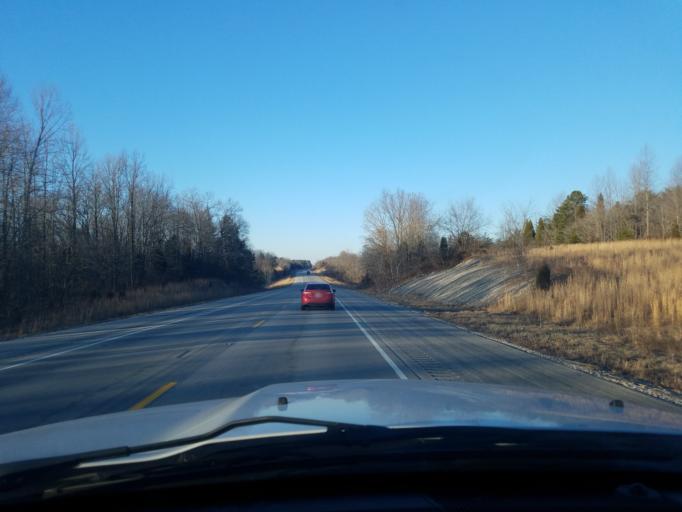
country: US
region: Indiana
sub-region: Crawford County
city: English
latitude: 38.1409
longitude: -86.6048
